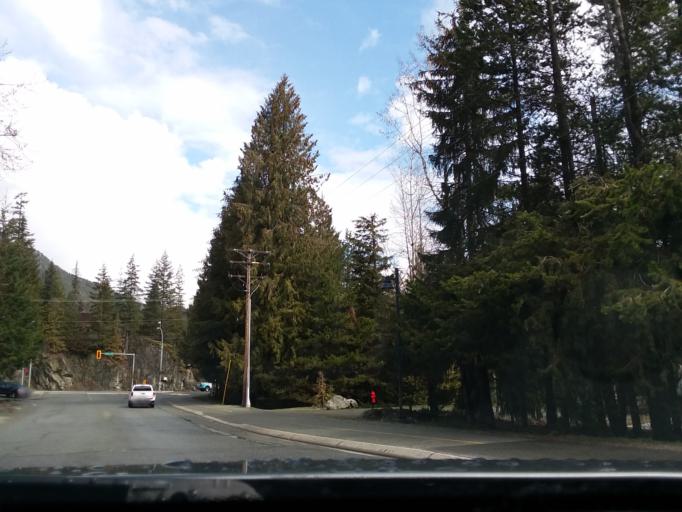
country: CA
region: British Columbia
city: Whistler
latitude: 50.0890
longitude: -122.9992
